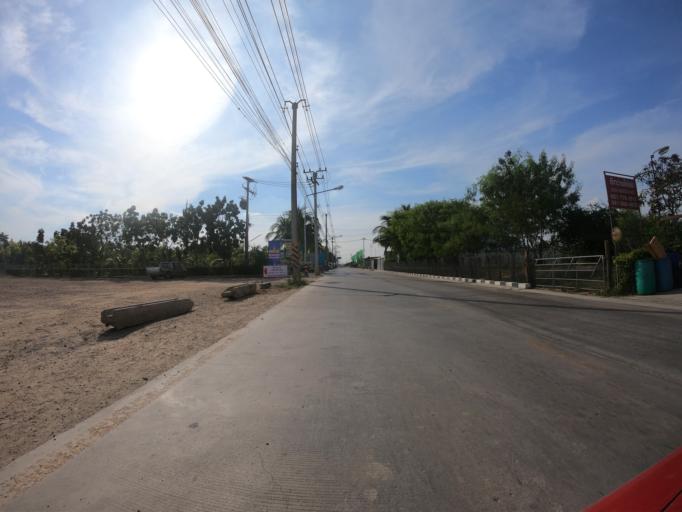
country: TH
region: Pathum Thani
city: Lam Luk Ka
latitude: 13.9613
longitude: 100.7224
